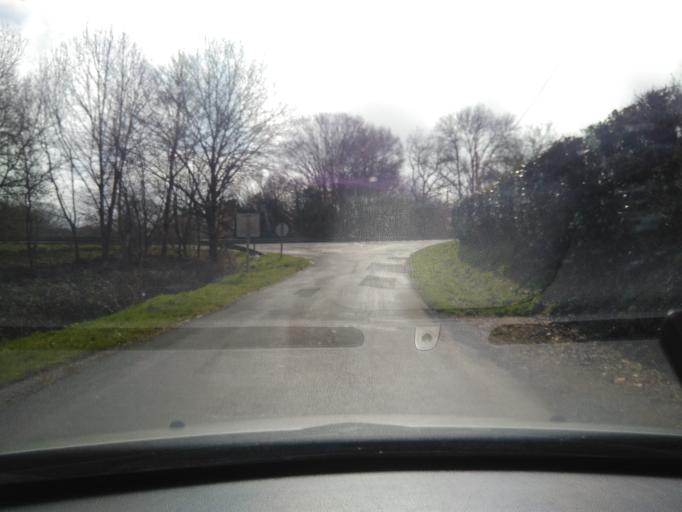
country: FR
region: Pays de la Loire
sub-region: Departement de la Vendee
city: Sainte-Cecile
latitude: 46.7008
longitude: -1.1256
